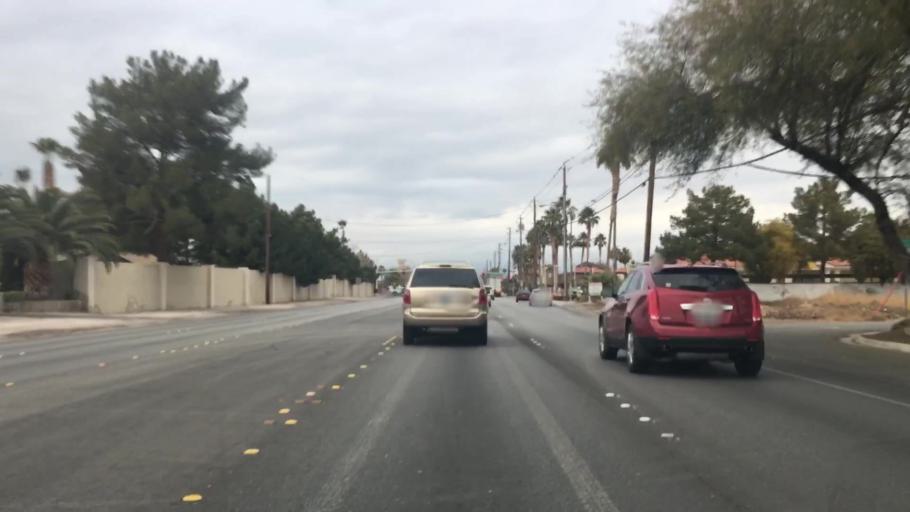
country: US
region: Nevada
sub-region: Clark County
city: Whitney
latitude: 36.0695
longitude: -115.1007
